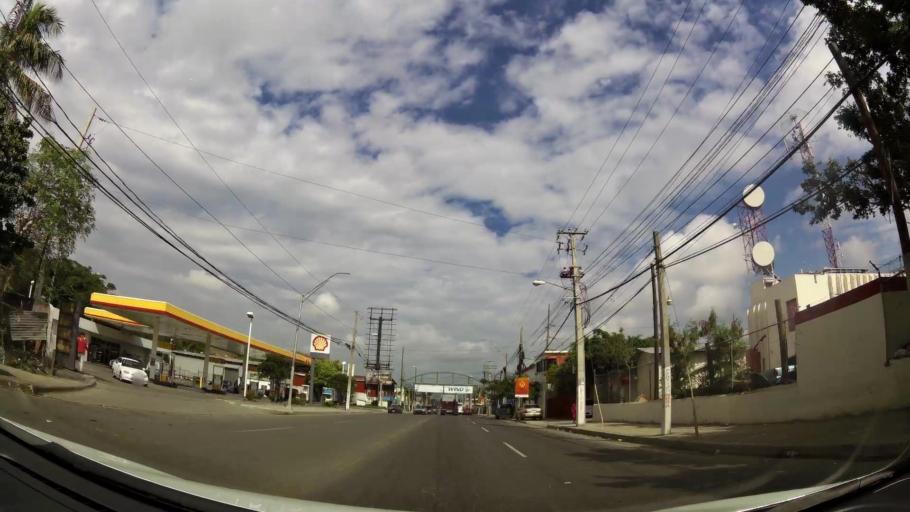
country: DO
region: Santiago
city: Santiago de los Caballeros
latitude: 19.4824
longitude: -70.7286
